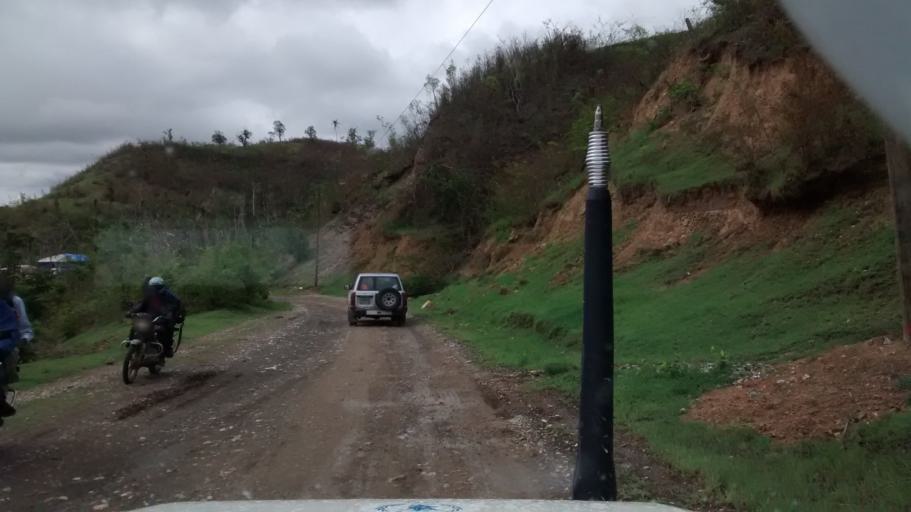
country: HT
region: Grandans
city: Jeremie
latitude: 18.5988
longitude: -74.1785
